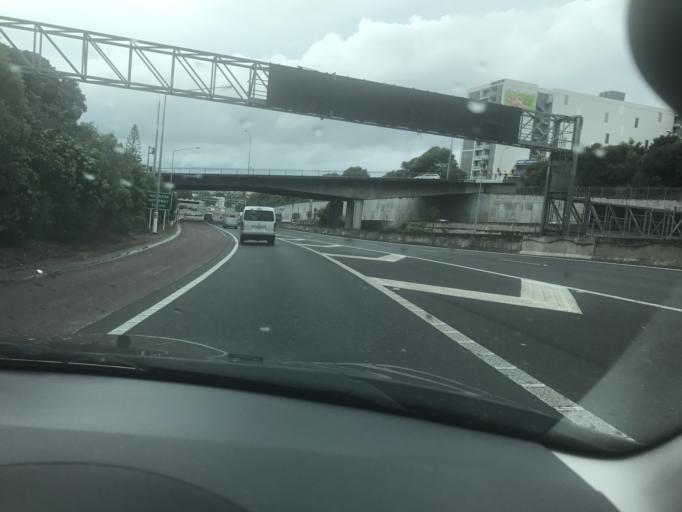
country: NZ
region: Auckland
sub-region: Auckland
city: Auckland
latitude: -36.8539
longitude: 174.7562
